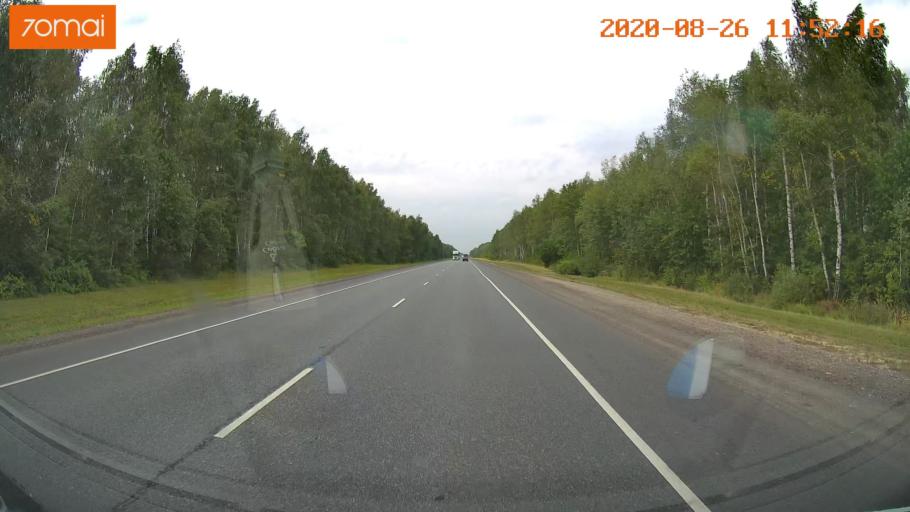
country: RU
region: Rjazan
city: Lesnoy
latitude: 54.2947
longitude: 40.4591
